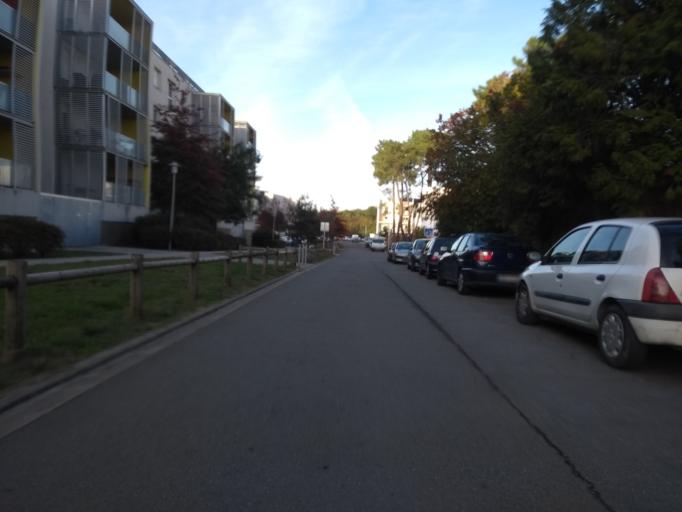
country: FR
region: Aquitaine
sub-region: Departement de la Gironde
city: Gradignan
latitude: 44.7851
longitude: -0.5989
